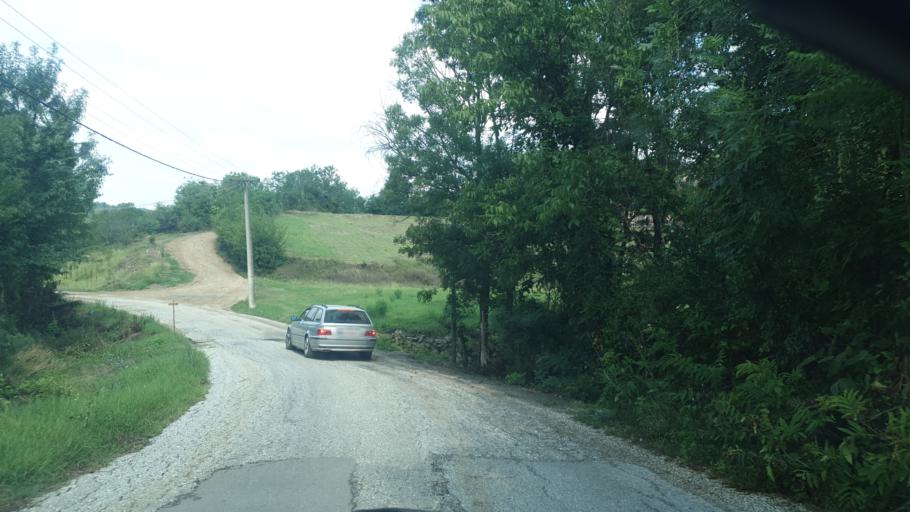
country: RS
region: Central Serbia
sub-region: Sumadijski Okrug
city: Kragujevac
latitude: 44.1048
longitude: 20.7883
